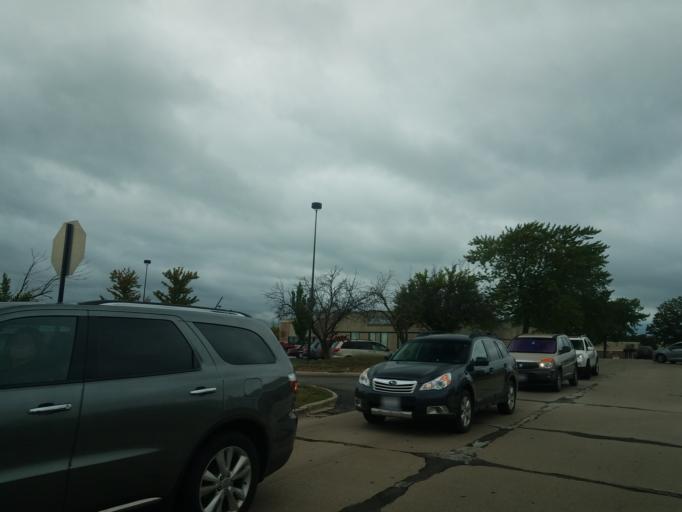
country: US
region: Illinois
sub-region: McLean County
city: Normal
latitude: 40.5097
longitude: -88.9556
